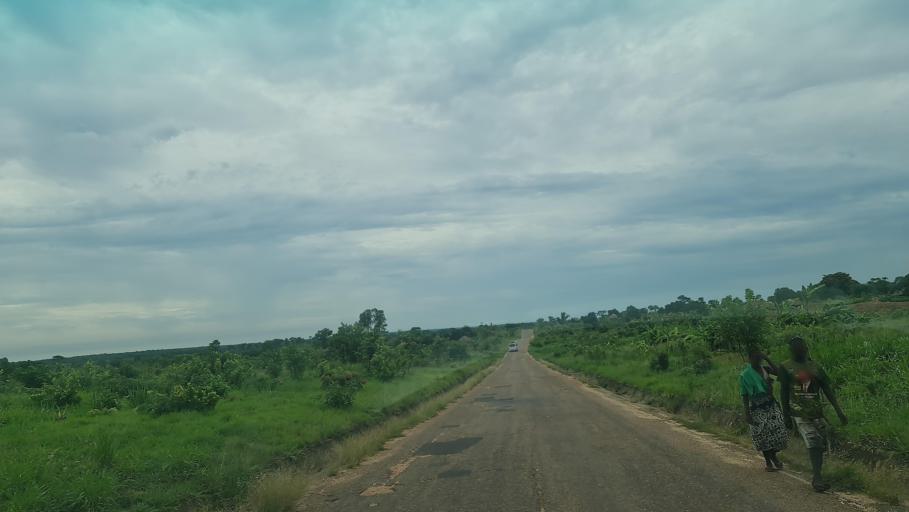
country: MW
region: Southern Region
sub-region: Nsanje District
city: Nsanje
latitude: -17.6778
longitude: 35.7222
